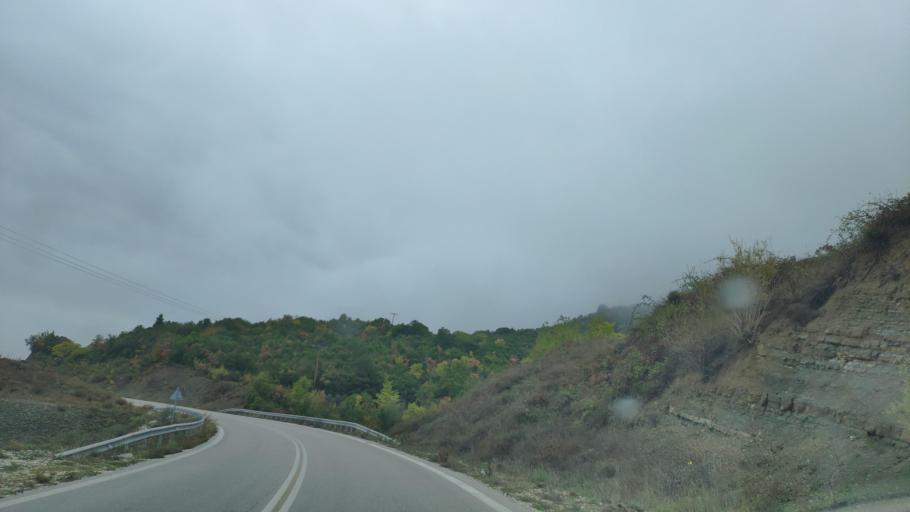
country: GR
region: Epirus
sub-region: Nomos Thesprotias
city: Paramythia
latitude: 39.4861
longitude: 20.6717
